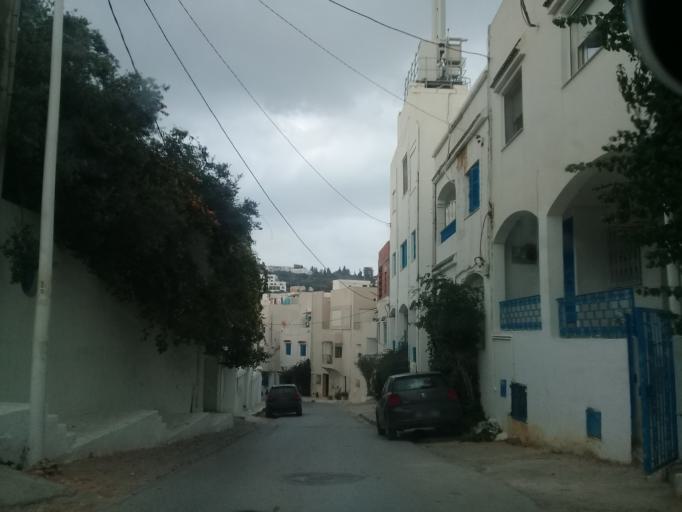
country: TN
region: Tunis
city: Sidi Bou Said
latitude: 36.8692
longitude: 10.3401
